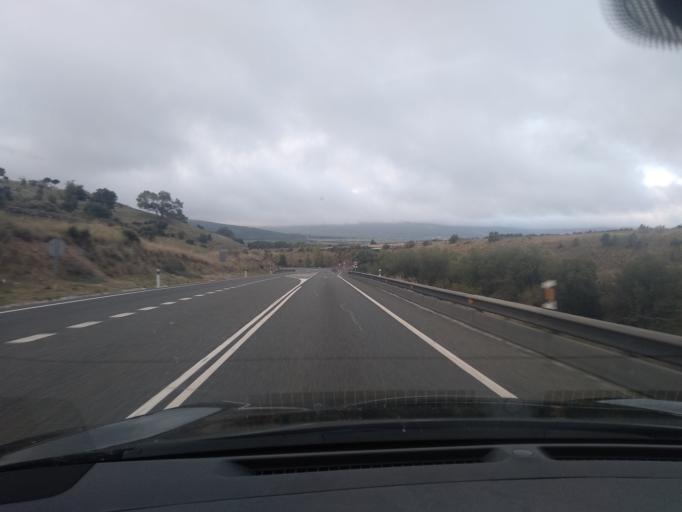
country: ES
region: Castille and Leon
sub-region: Provincia de Segovia
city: Otero de Herreros
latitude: 40.7607
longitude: -4.2107
